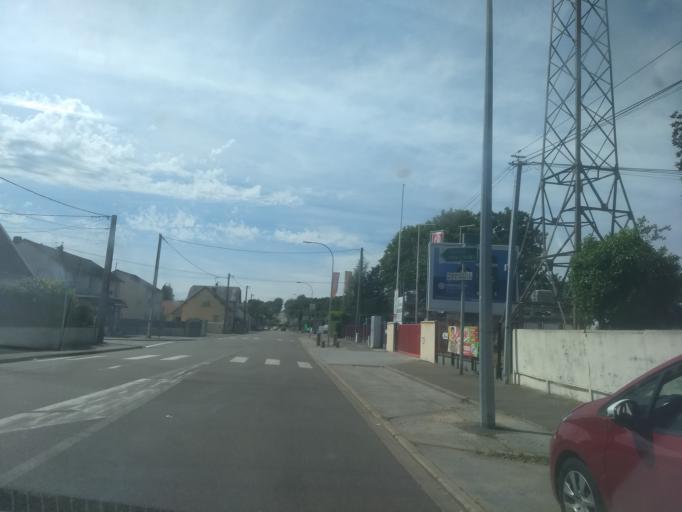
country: FR
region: Centre
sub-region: Departement d'Eure-et-Loir
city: Nogent-le-Rotrou
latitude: 48.3272
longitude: 0.8049
